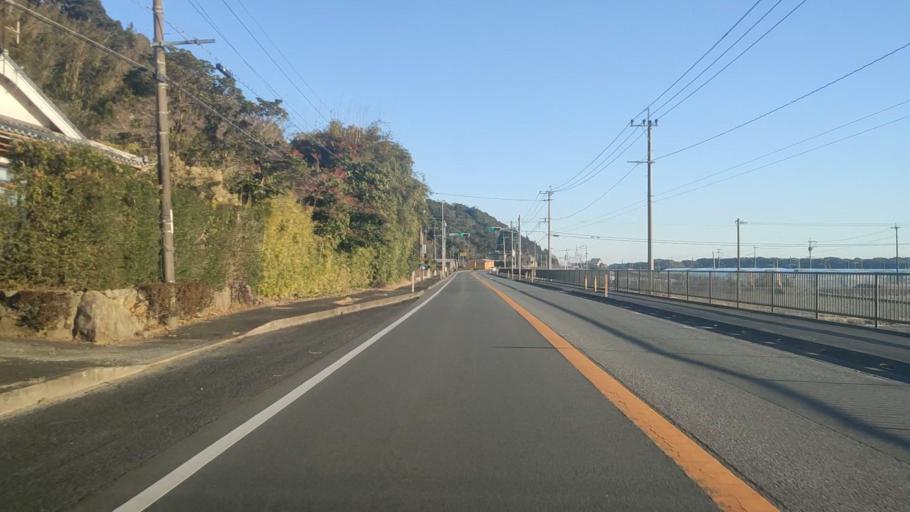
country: JP
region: Miyazaki
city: Takanabe
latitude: 32.0921
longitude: 131.5151
